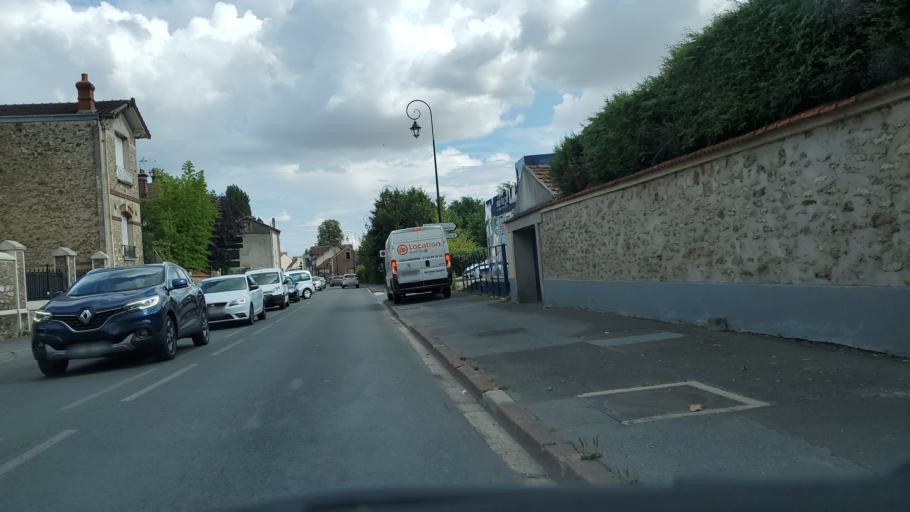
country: FR
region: Ile-de-France
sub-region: Departement de Seine-et-Marne
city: Coulommiers
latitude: 48.8124
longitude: 3.0767
